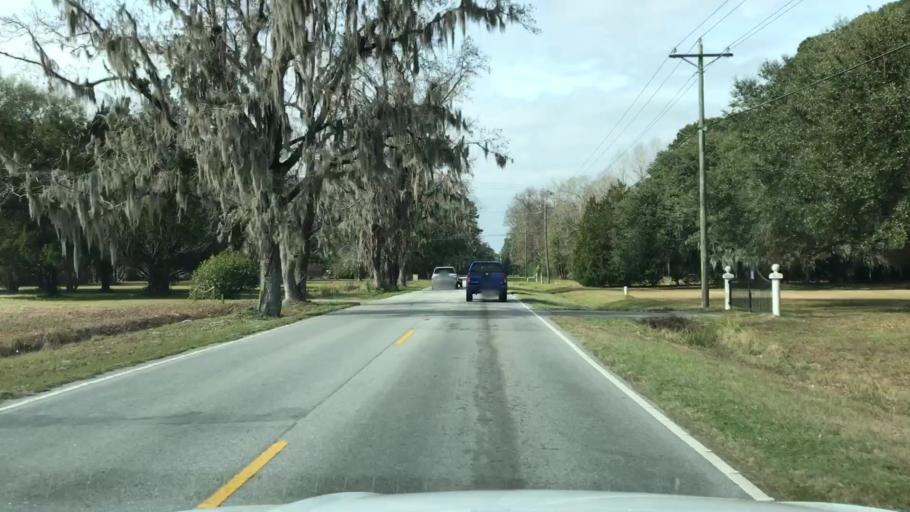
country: US
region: South Carolina
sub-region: Charleston County
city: Shell Point
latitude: 32.7785
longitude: -80.0992
